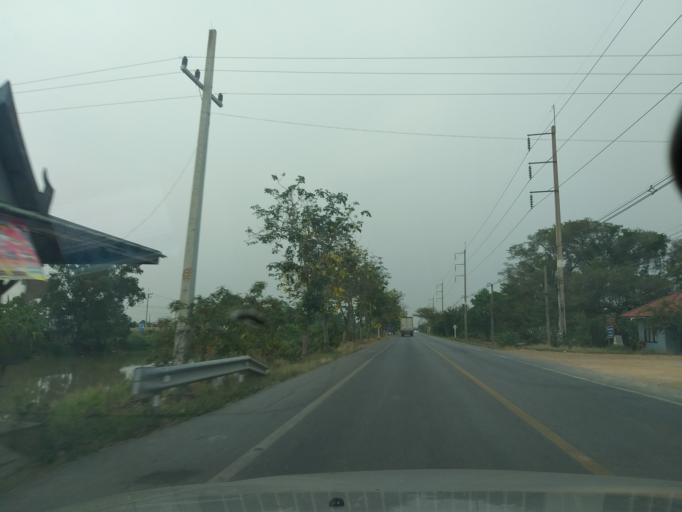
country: TH
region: Pathum Thani
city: Ban Lam Luk Ka
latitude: 13.9846
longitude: 100.8953
